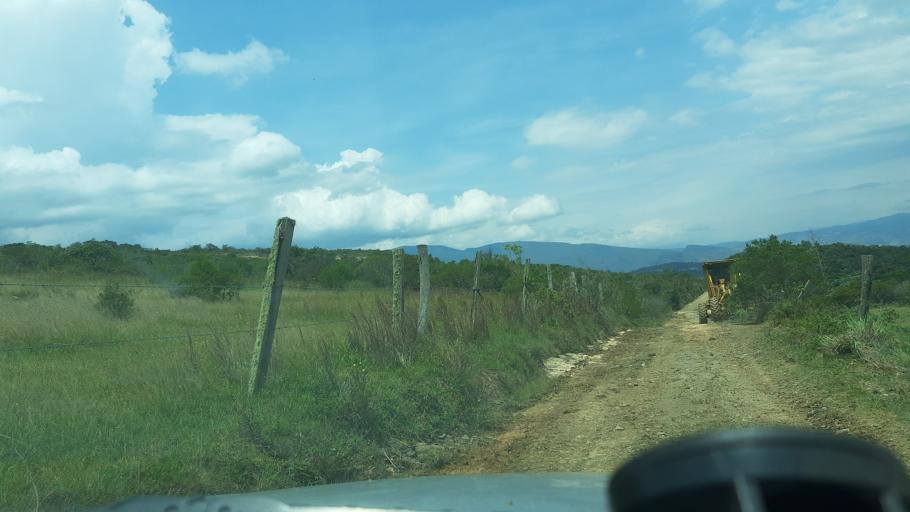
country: CO
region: Boyaca
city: Santa Sofia
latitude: 5.7031
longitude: -73.5817
